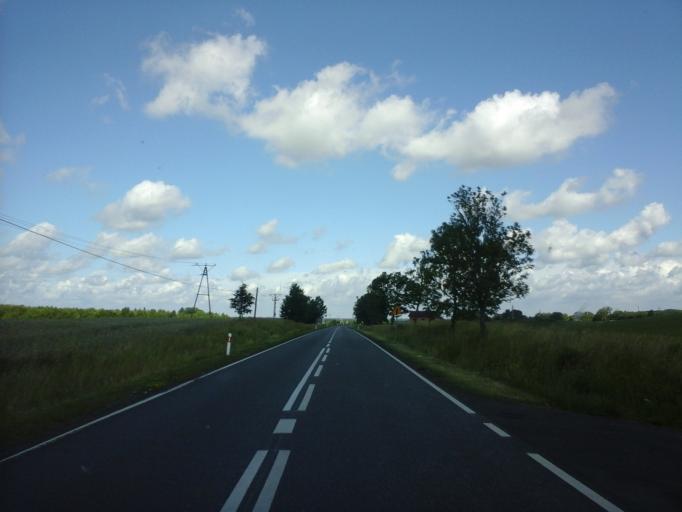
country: PL
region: West Pomeranian Voivodeship
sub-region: Powiat lobeski
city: Wegorzyno
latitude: 53.5262
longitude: 15.5644
